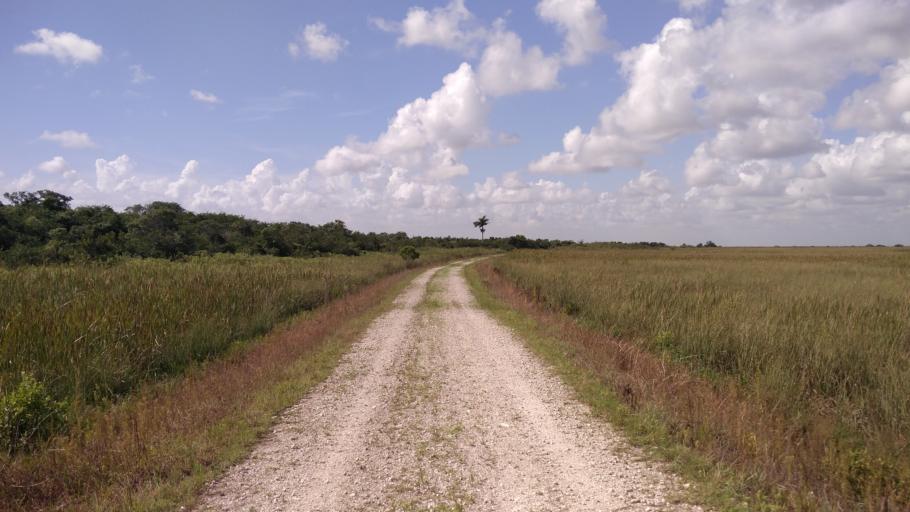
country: US
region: Florida
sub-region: Broward County
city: Weston
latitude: 26.0528
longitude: -80.4618
